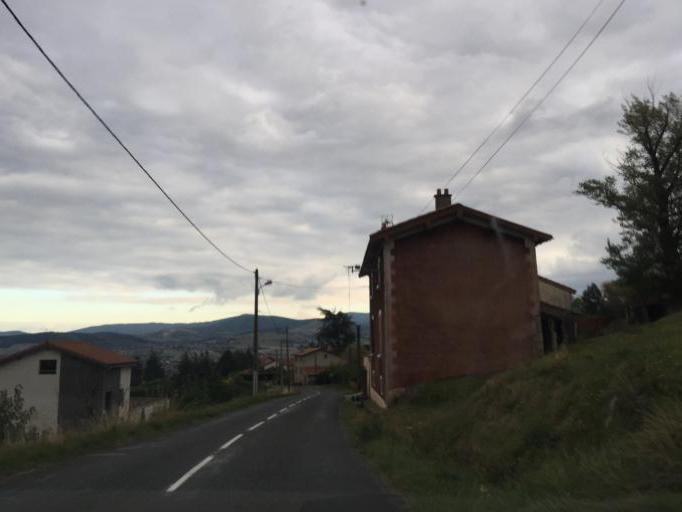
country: FR
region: Rhone-Alpes
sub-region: Departement de la Loire
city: Cellieu
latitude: 45.5176
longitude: 4.5558
